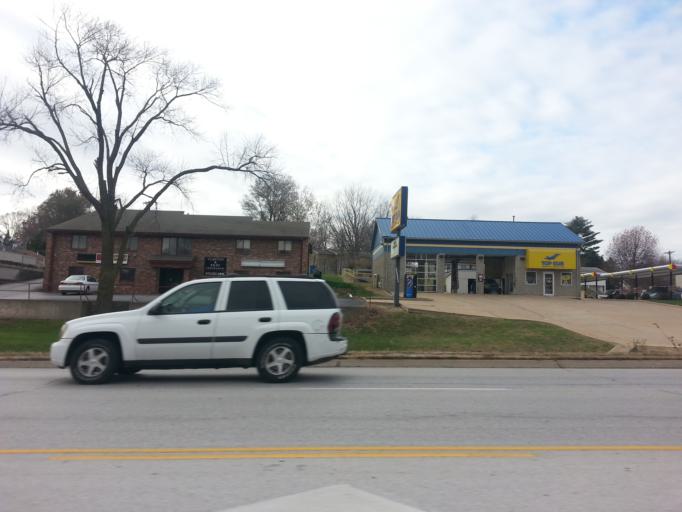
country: US
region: Missouri
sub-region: Marion County
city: Hannibal
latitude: 39.7173
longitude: -91.3920
